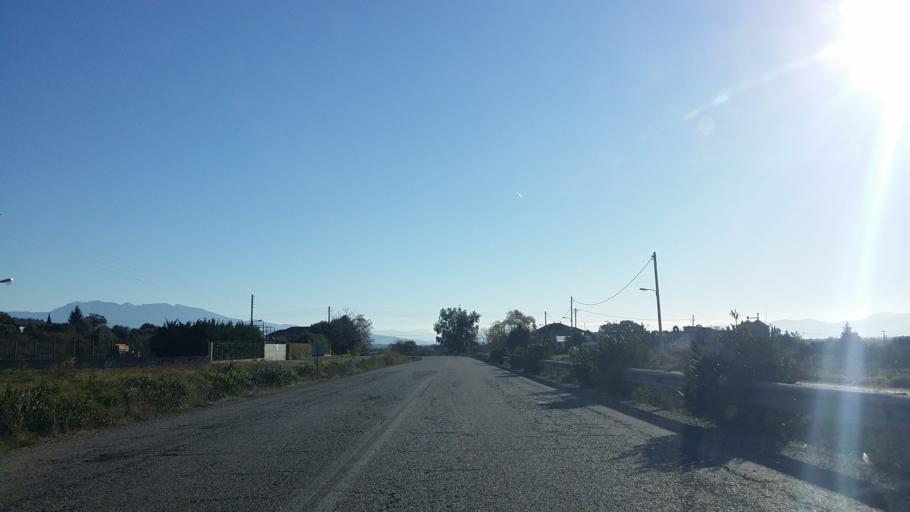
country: GR
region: West Greece
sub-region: Nomos Aitolias kai Akarnanias
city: Fitiai
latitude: 38.6883
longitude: 21.2318
